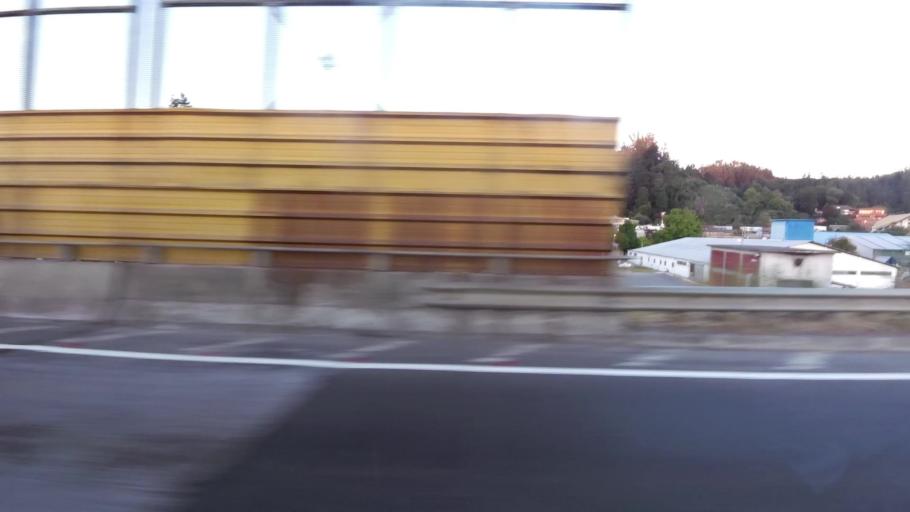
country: CL
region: Biobio
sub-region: Provincia de Concepcion
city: Concepcion
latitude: -36.8478
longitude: -73.0547
